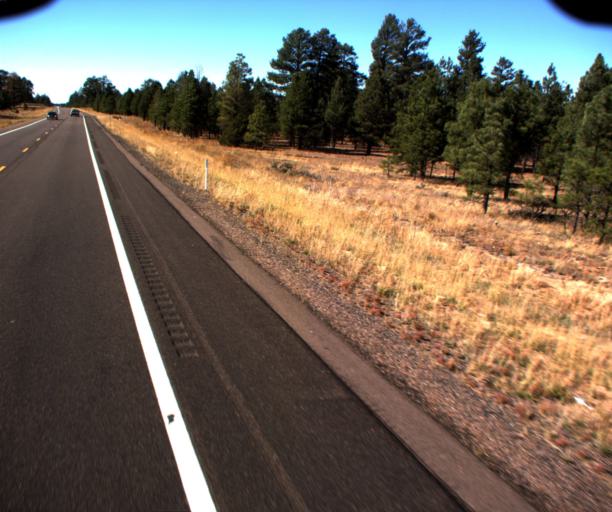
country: US
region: Arizona
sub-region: Apache County
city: Saint Michaels
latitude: 35.6968
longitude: -109.2769
